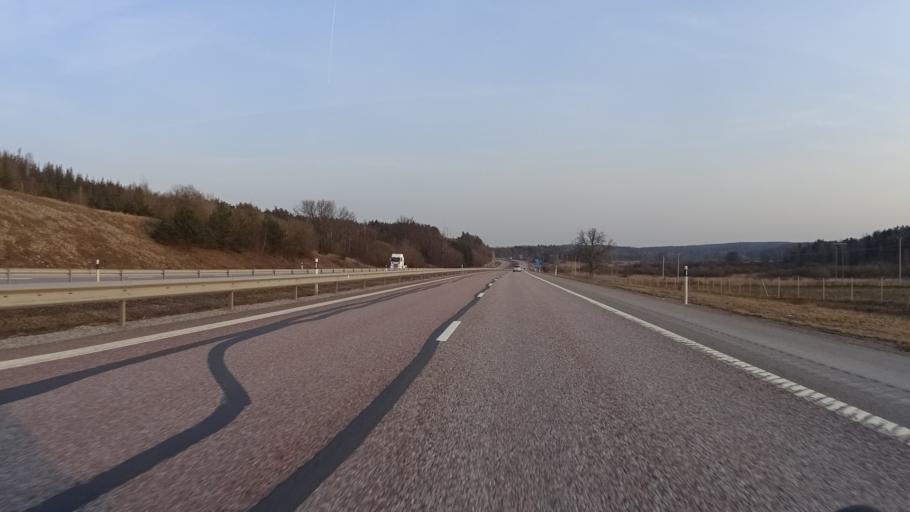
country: SE
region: Soedermanland
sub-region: Strangnas Kommun
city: Akers Styckebruk
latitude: 59.2605
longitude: 17.1457
